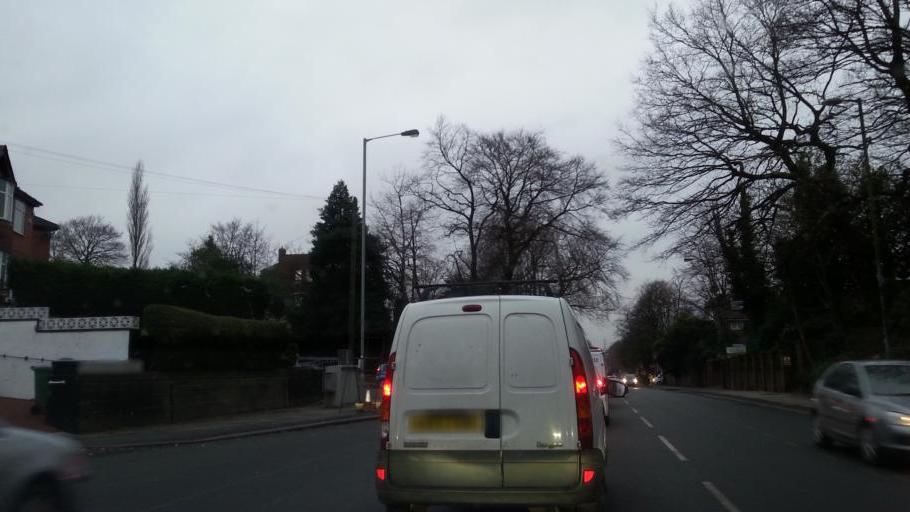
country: GB
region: England
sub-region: Borough of Bury
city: Prestwich
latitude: 53.5252
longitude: -2.2779
